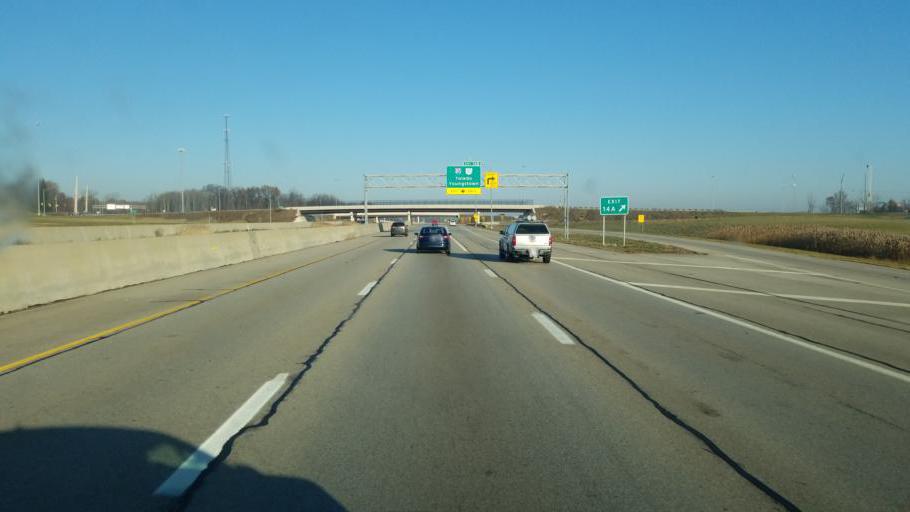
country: US
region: Ohio
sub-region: Summit County
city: Boston Heights
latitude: 41.2520
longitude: -81.4990
